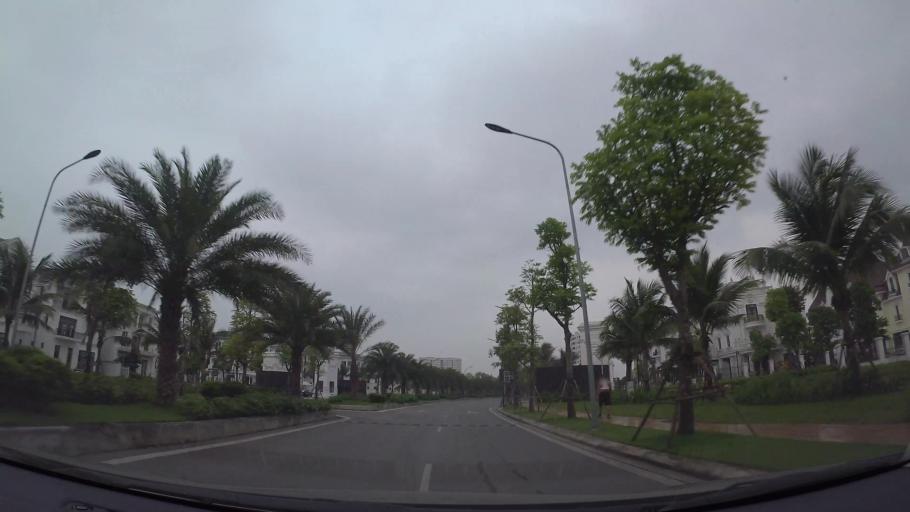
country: VN
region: Ha Noi
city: Trau Quy
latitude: 21.0424
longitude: 105.9075
